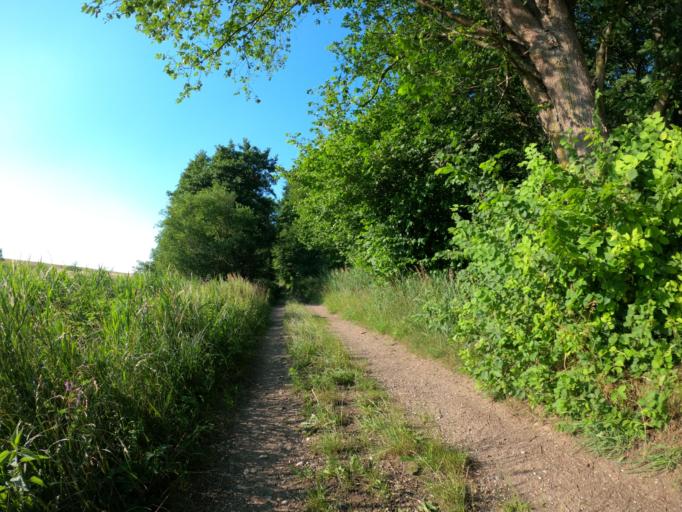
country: DE
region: Brandenburg
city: Gartz
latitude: 53.2346
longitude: 14.3664
